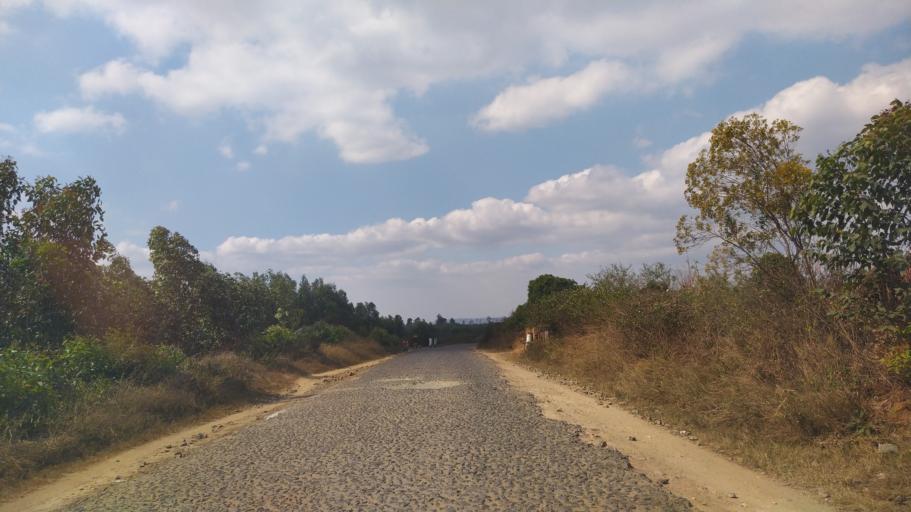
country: MG
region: Alaotra Mangoro
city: Moramanga
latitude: -18.7695
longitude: 48.2516
